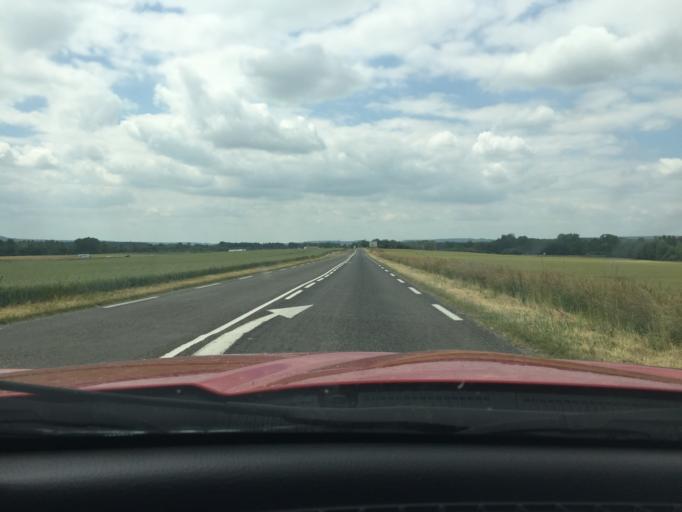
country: FR
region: Champagne-Ardenne
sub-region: Departement de la Marne
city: Cormicy
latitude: 49.4134
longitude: 3.8939
